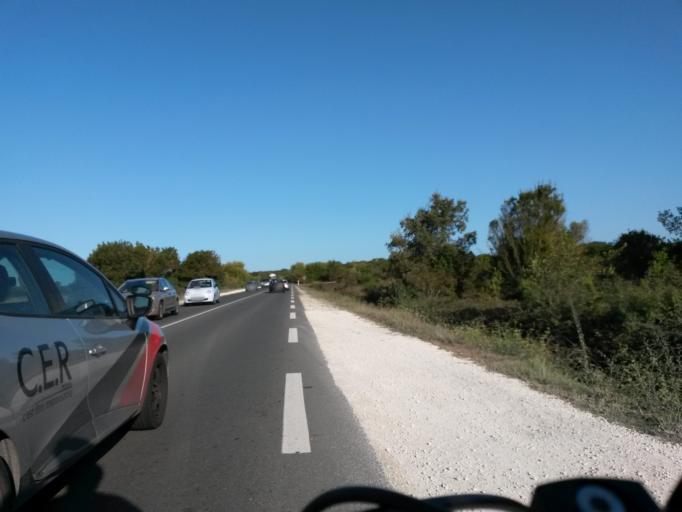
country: FR
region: Poitou-Charentes
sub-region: Departement de la Charente-Maritime
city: Rivedoux-Plage
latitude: 46.1514
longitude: -1.2775
